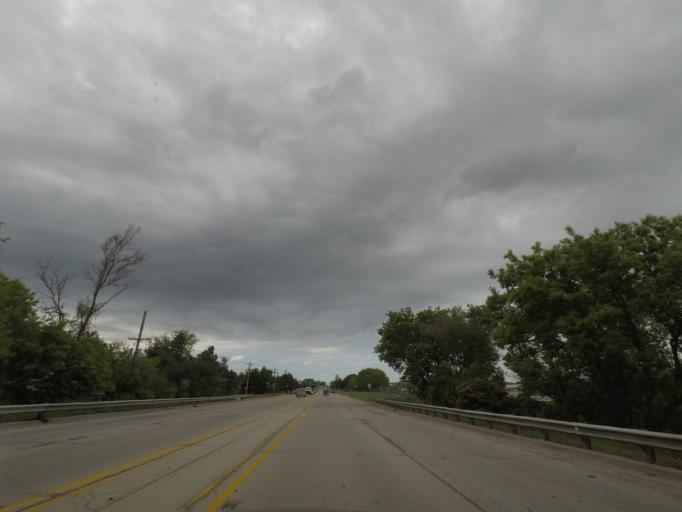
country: US
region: Illinois
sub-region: Winnebago County
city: Rockford
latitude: 42.2323
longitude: -89.0289
